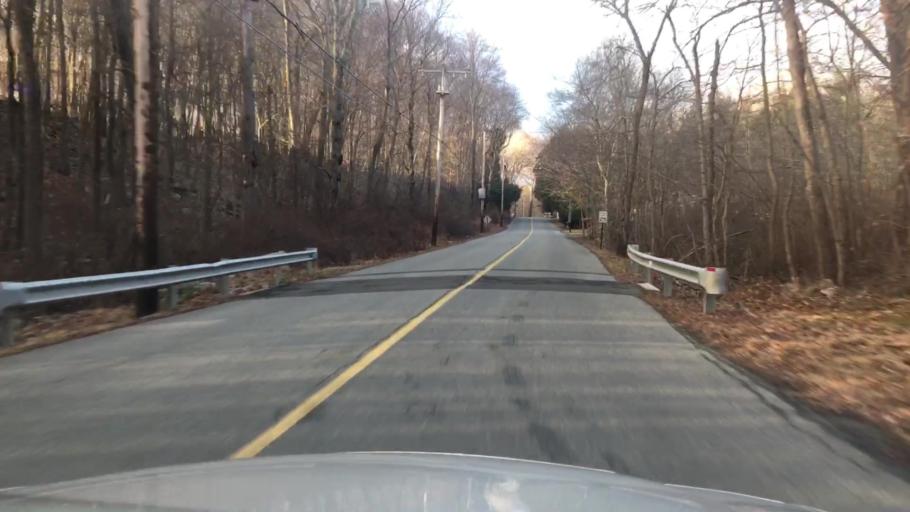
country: US
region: Connecticut
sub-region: Middlesex County
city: Essex Village
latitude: 41.3721
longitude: -72.4065
